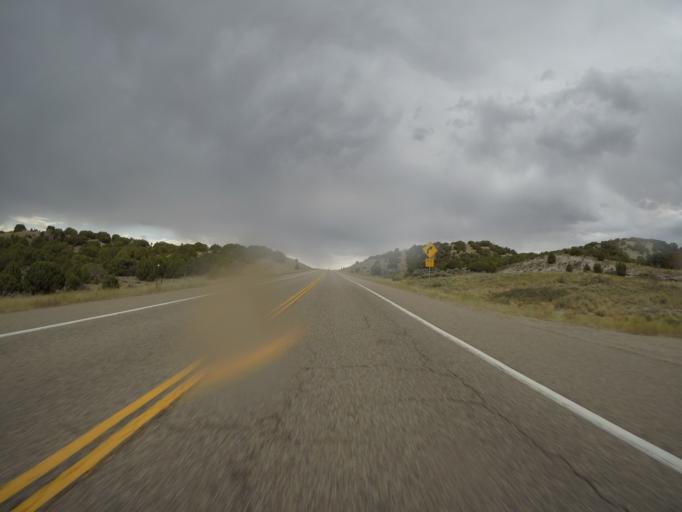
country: US
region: Colorado
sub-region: Rio Blanco County
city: Meeker
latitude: 40.4106
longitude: -108.3357
